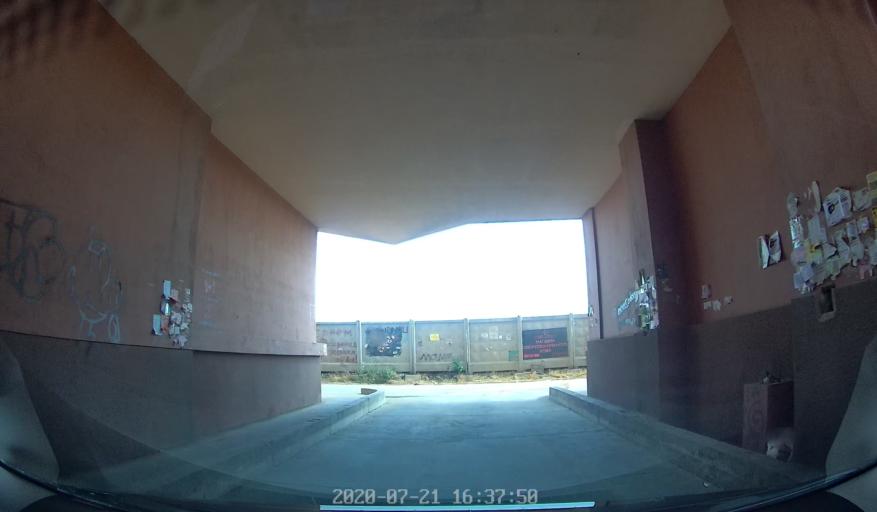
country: TR
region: Kirklareli
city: Sergen
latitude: 41.7606
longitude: 27.6346
